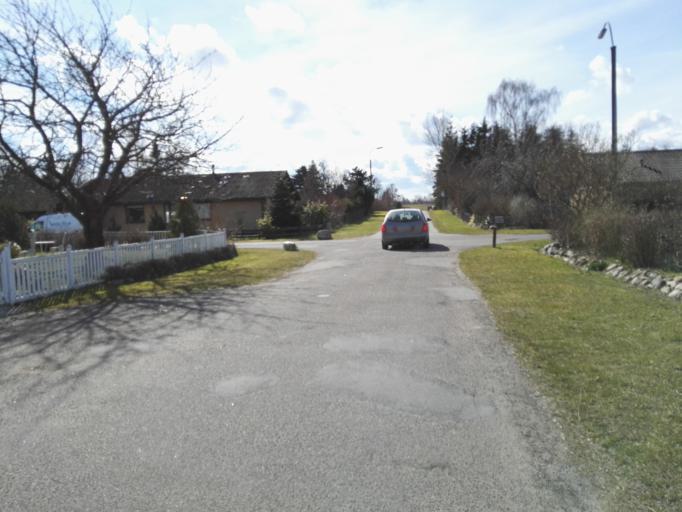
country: DK
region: Zealand
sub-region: Lejre Kommune
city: Ejby
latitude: 55.7674
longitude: 11.8026
